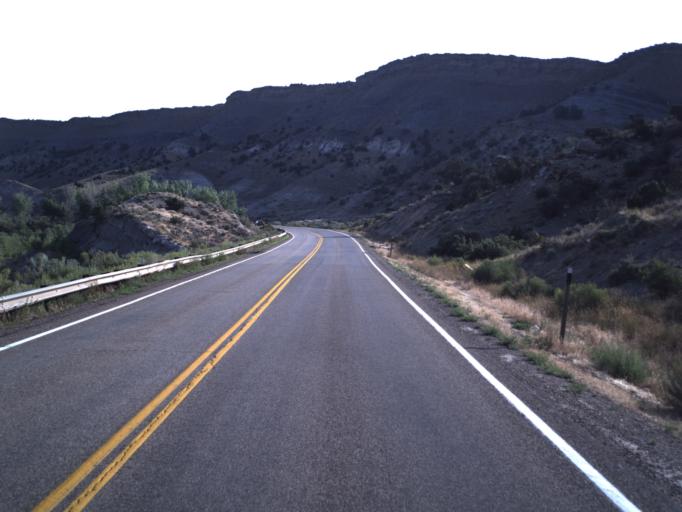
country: US
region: Utah
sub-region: Uintah County
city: Vernal
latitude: 40.5174
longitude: -109.5235
